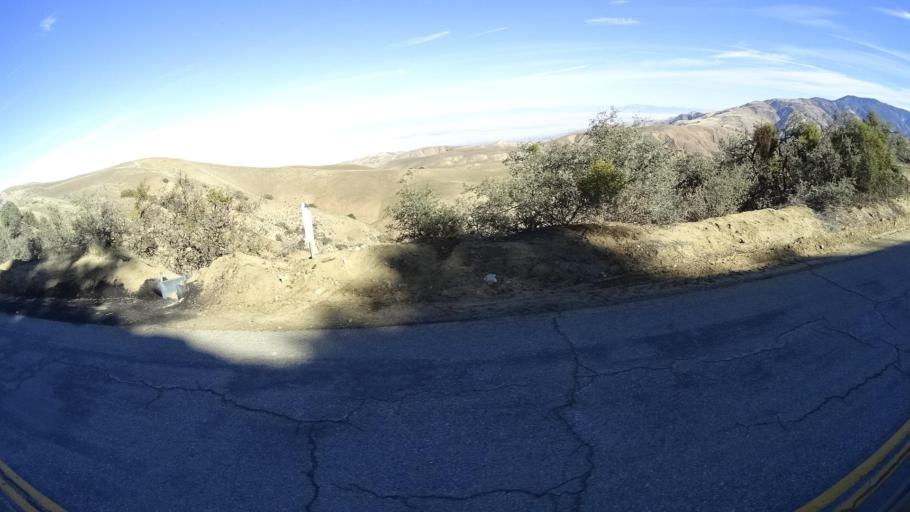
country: US
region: California
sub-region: Kern County
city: Maricopa
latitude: 34.8956
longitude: -119.3645
